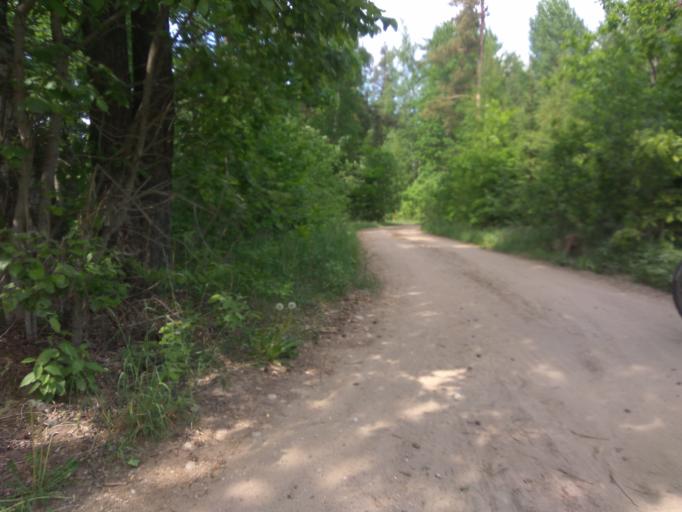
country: LV
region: Kuldigas Rajons
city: Kuldiga
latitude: 56.8983
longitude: 21.9219
